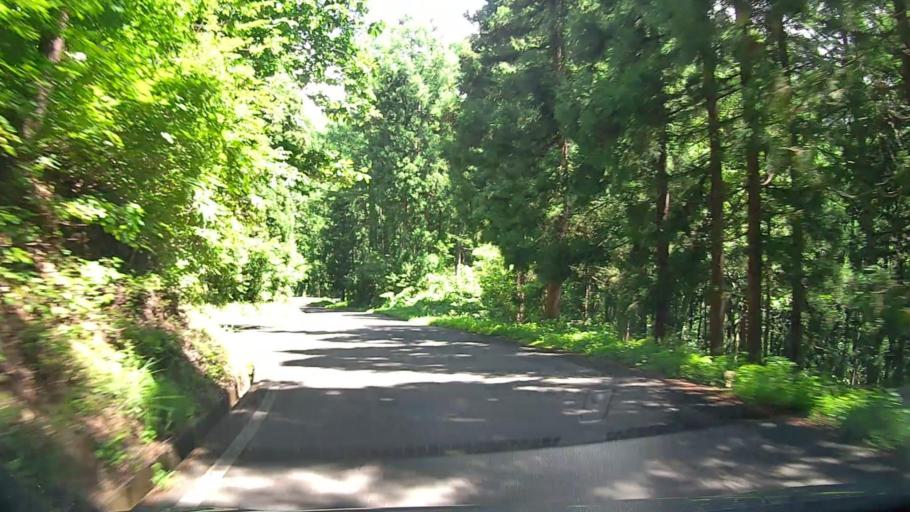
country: JP
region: Nagano
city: Iiyama
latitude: 36.9299
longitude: 138.4504
